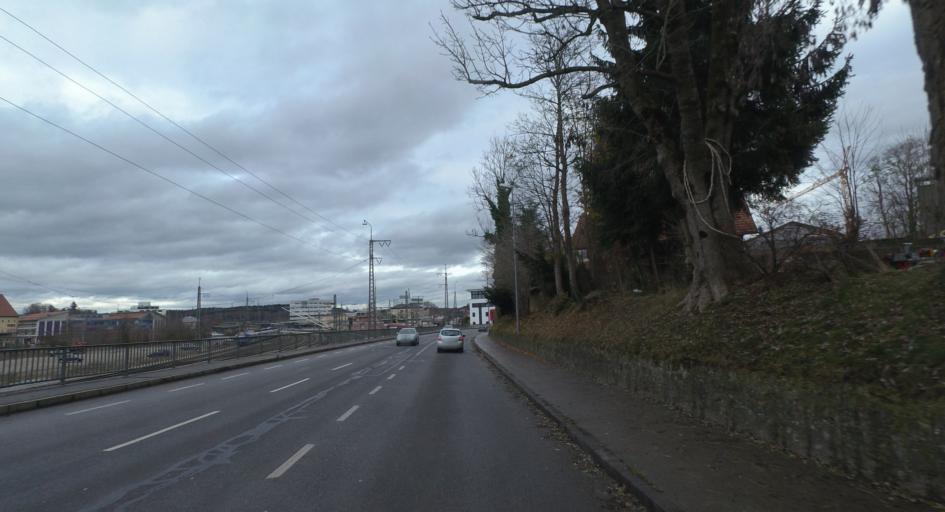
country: DE
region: Bavaria
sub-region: Upper Bavaria
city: Traunstein
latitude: 47.8685
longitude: 12.6346
